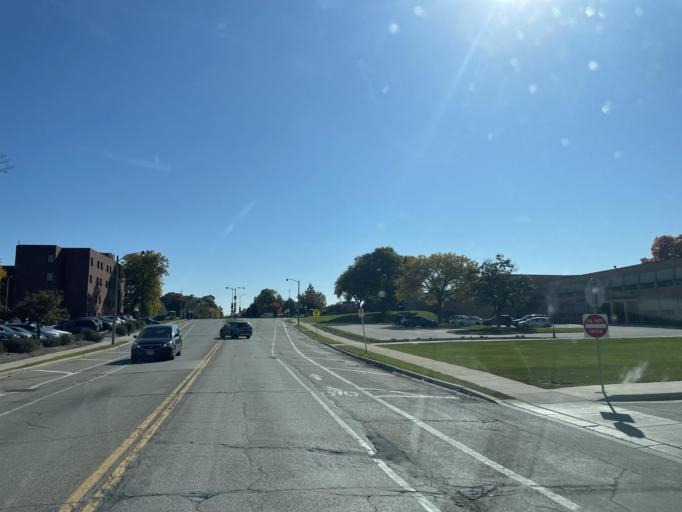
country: US
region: Wisconsin
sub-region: Milwaukee County
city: Wauwatosa
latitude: 43.0625
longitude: -88.0075
